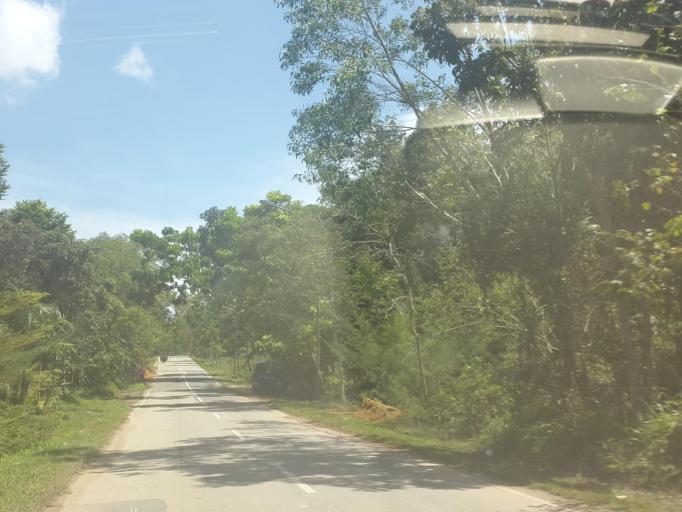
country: SG
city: Singapore
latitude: 1.0805
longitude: 103.9546
